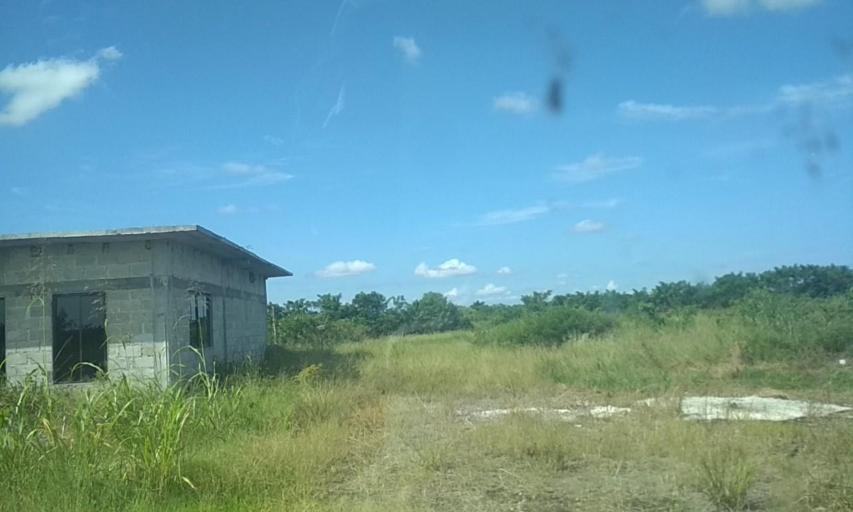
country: MX
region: Veracruz
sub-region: Martinez de la Torre
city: La Union Paso Largo
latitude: 20.1340
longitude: -96.9903
